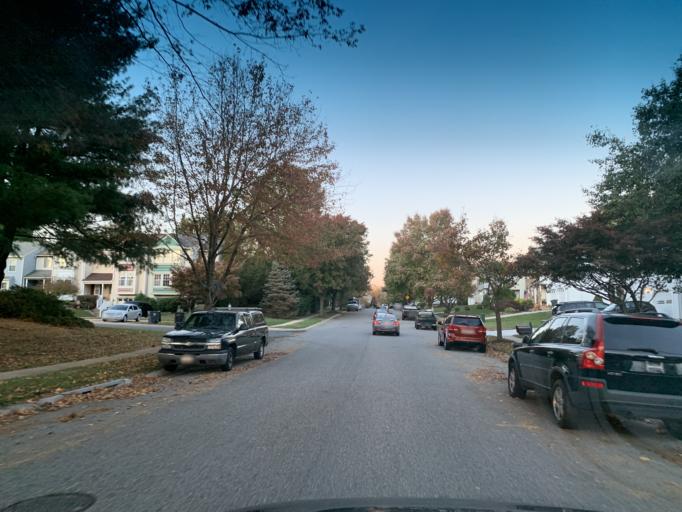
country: US
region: Maryland
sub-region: Harford County
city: Bel Air South
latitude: 39.5334
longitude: -76.3054
